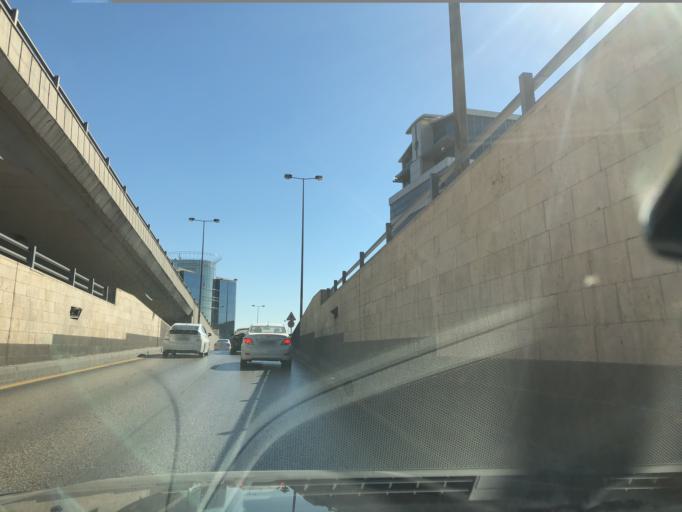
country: JO
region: Amman
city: Wadi as Sir
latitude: 31.9762
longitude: 35.8542
